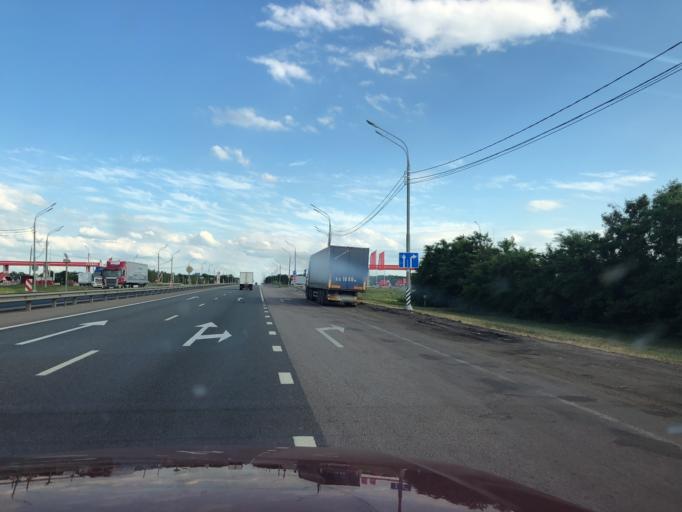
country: RU
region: Lipetsk
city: Zadonsk
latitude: 52.4277
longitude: 38.8275
